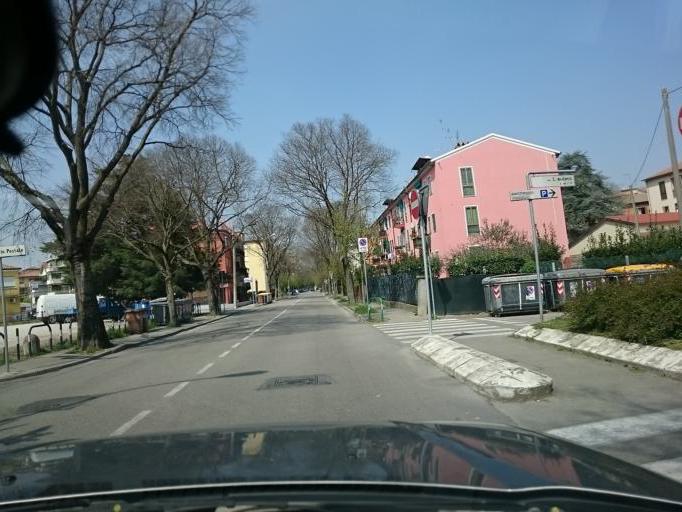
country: IT
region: Veneto
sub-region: Provincia di Padova
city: Caselle
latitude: 45.3980
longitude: 11.8329
